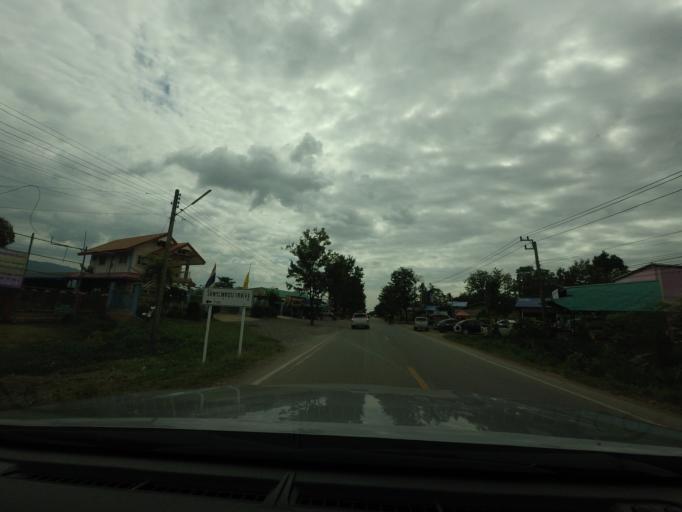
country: TH
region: Phitsanulok
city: Noen Maprang
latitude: 16.6718
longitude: 100.6142
